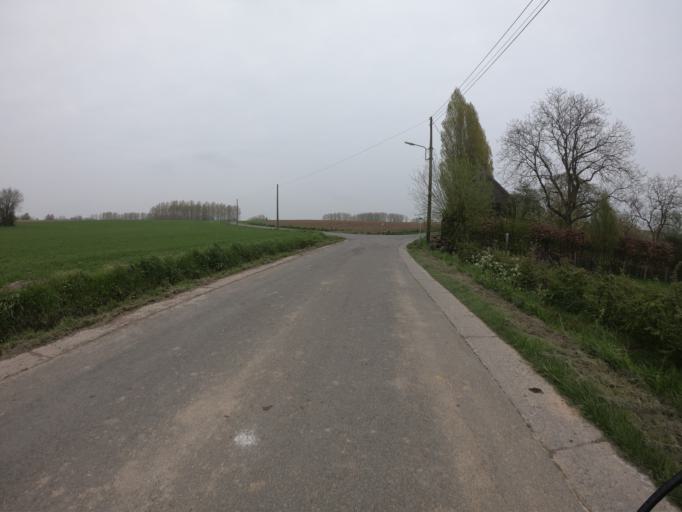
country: BE
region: Wallonia
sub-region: Province du Hainaut
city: Flobecq
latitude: 50.7494
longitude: 3.7713
